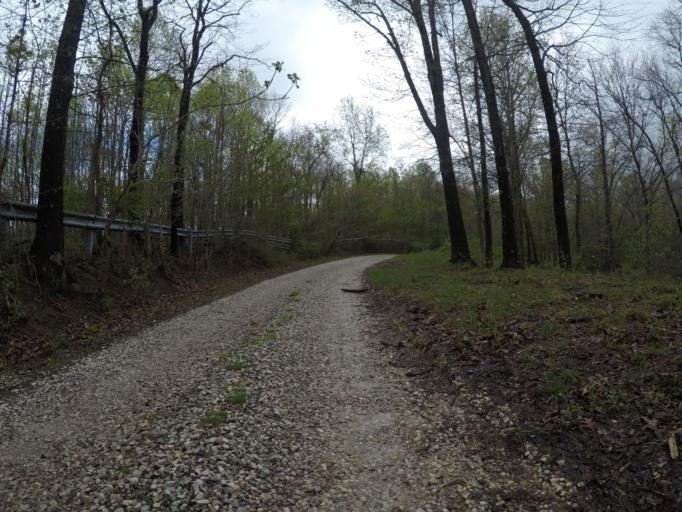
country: US
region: West Virginia
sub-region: Cabell County
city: Huntington
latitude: 38.3864
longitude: -82.4821
